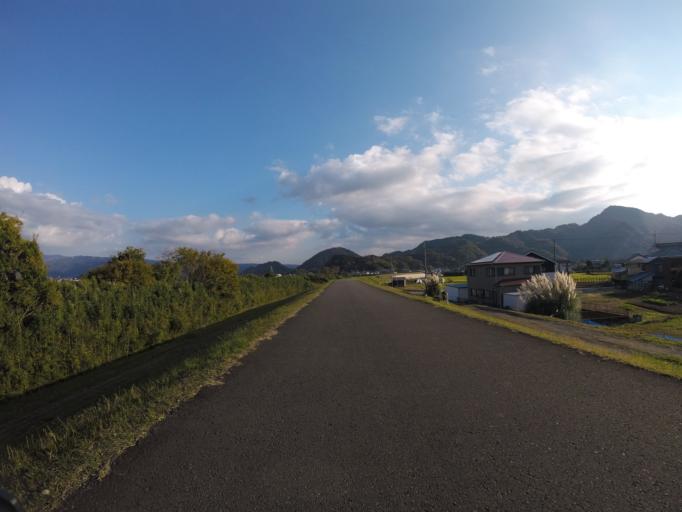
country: JP
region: Shizuoka
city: Mishima
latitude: 35.0786
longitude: 138.9121
